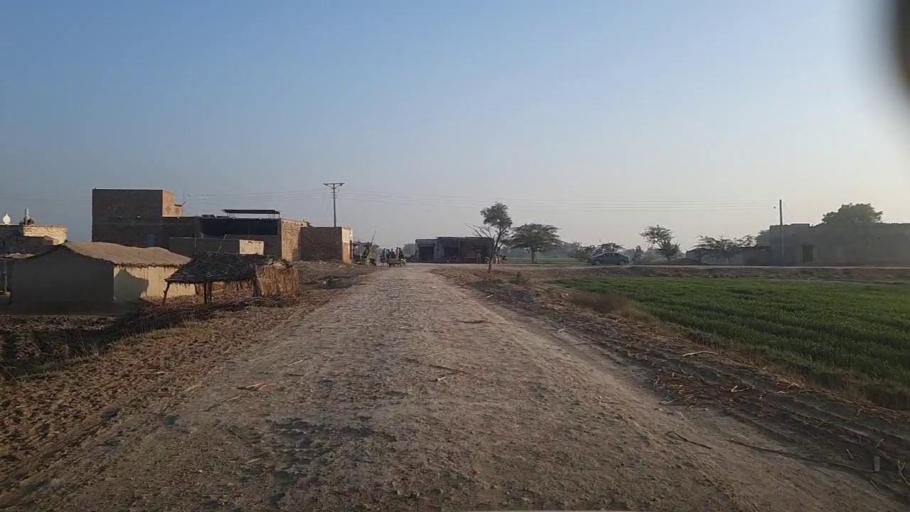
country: PK
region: Sindh
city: Khairpur
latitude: 28.0650
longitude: 69.7523
